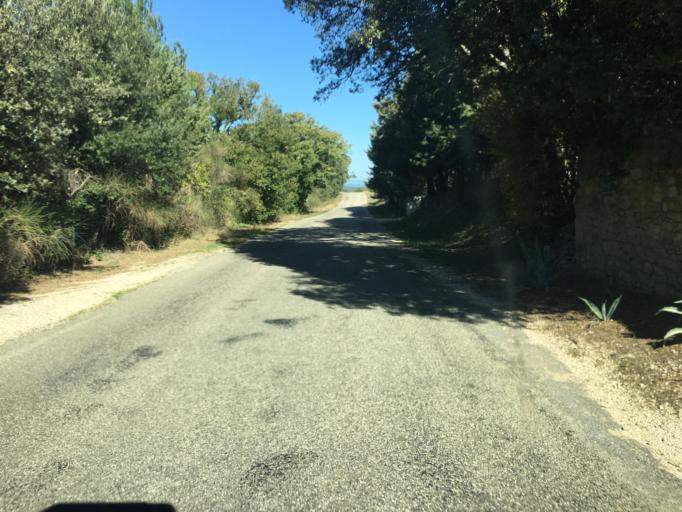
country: FR
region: Languedoc-Roussillon
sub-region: Departement du Gard
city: Barjac
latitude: 44.1724
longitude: 4.3217
